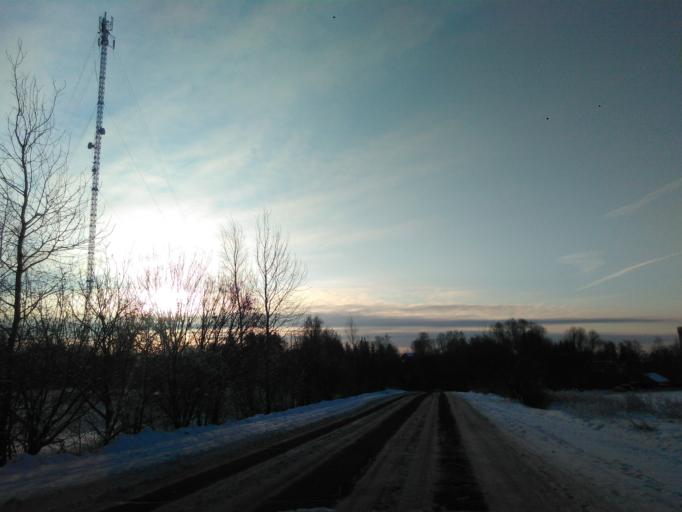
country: RU
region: Tverskaya
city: Zavidovo
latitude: 56.6148
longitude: 36.6182
